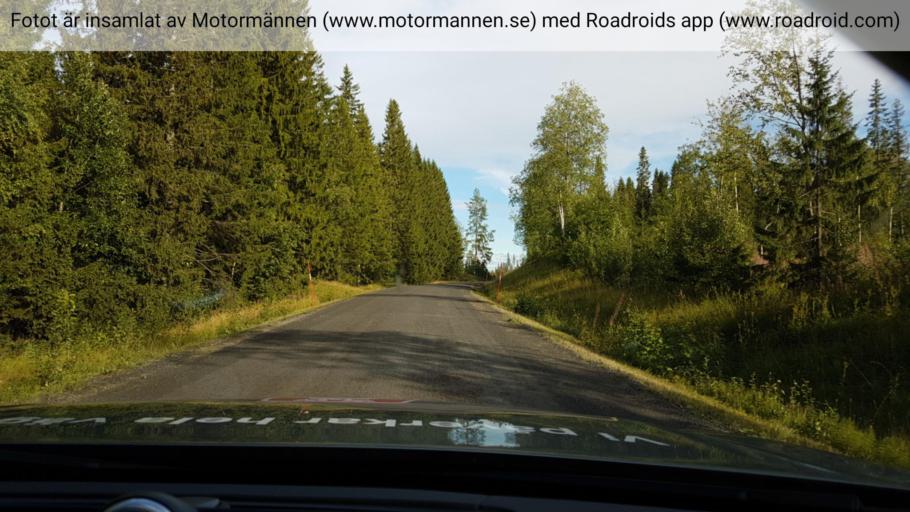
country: SE
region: Jaemtland
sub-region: Stroemsunds Kommun
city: Stroemsund
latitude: 64.1315
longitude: 15.7868
